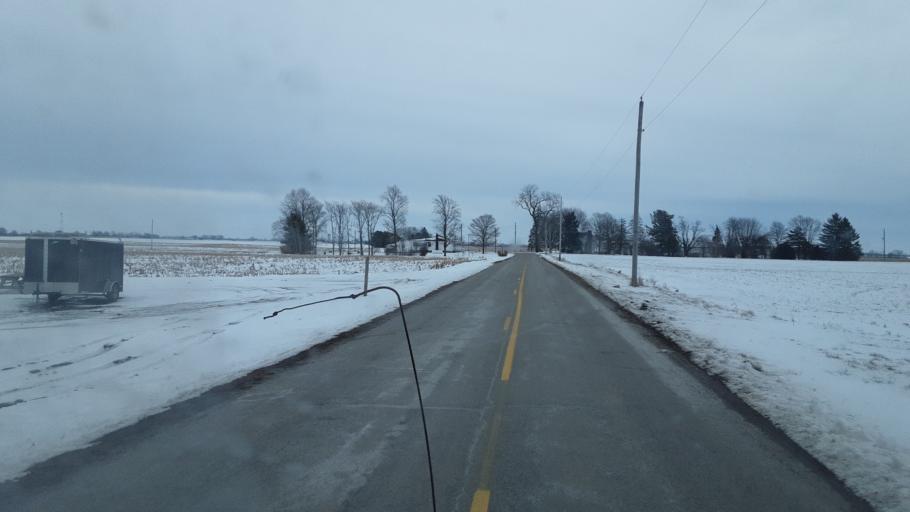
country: US
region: Ohio
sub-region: Madison County
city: Mount Sterling
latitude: 39.7144
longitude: -83.3151
